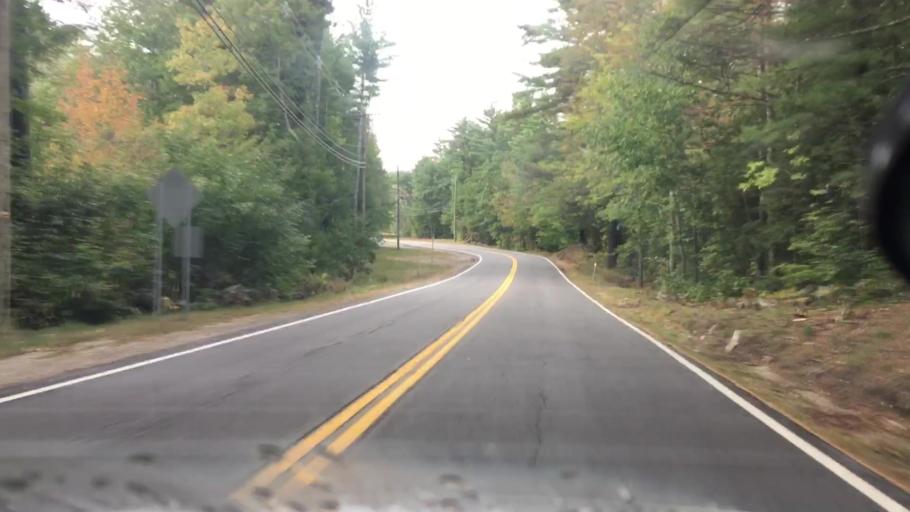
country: US
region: New Hampshire
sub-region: Carroll County
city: Wakefield
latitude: 43.5625
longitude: -71.0281
